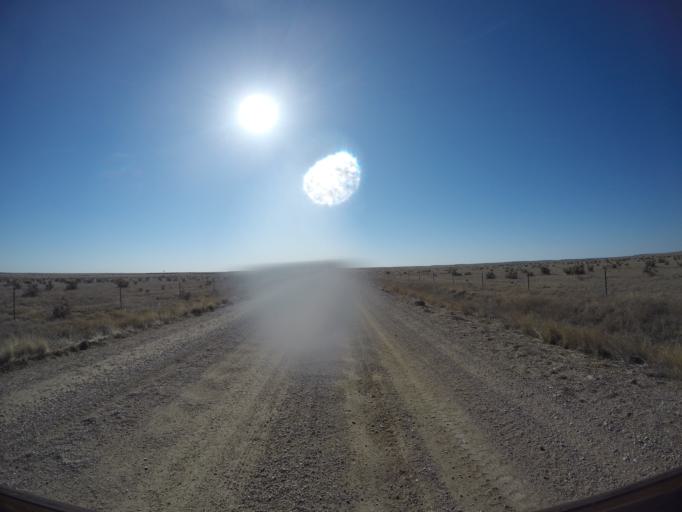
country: US
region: Colorado
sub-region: Otero County
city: La Junta
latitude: 37.7089
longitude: -103.6205
